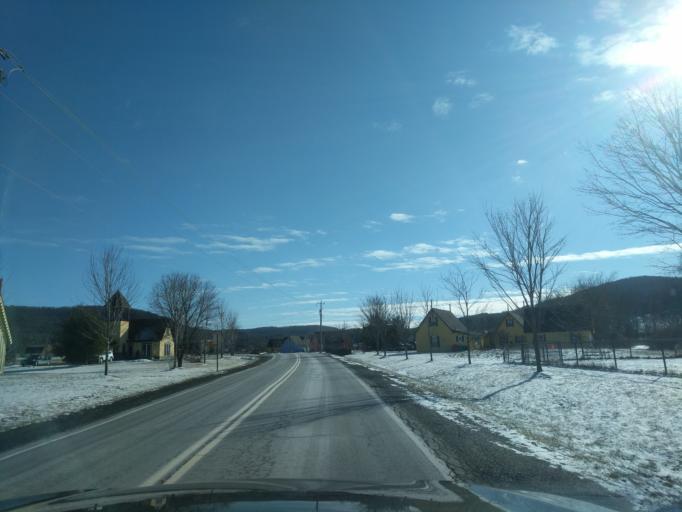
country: US
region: New York
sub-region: Tompkins County
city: Dryden
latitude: 42.3888
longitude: -76.3623
